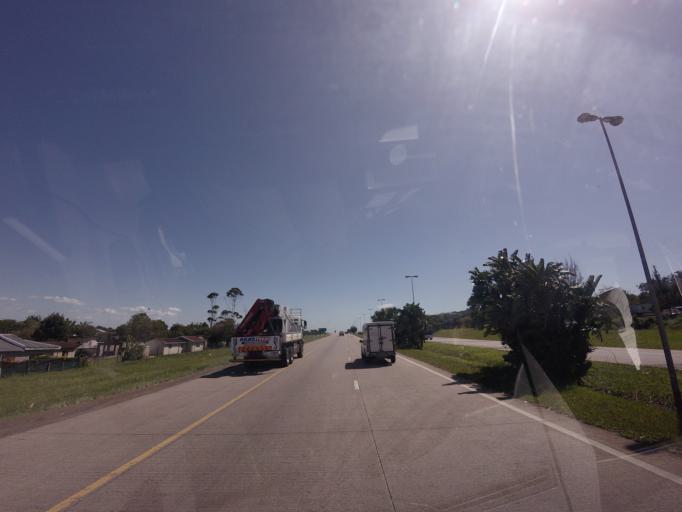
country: ZA
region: KwaZulu-Natal
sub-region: iLembe District Municipality
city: Stanger
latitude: -29.4014
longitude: 31.2868
